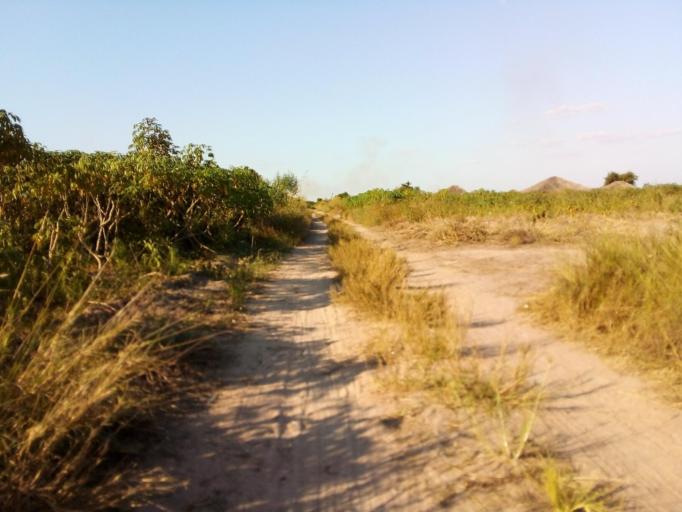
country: MZ
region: Zambezia
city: Quelimane
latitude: -17.5507
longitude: 36.7069
